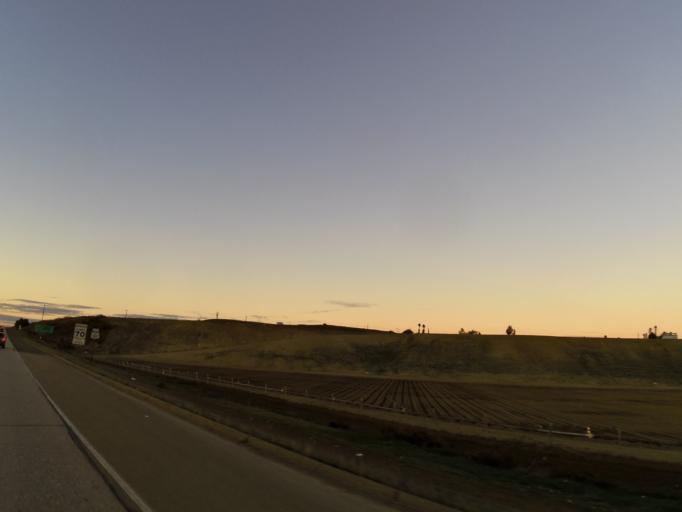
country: US
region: California
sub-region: Monterey County
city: King City
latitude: 36.1261
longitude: -121.0259
